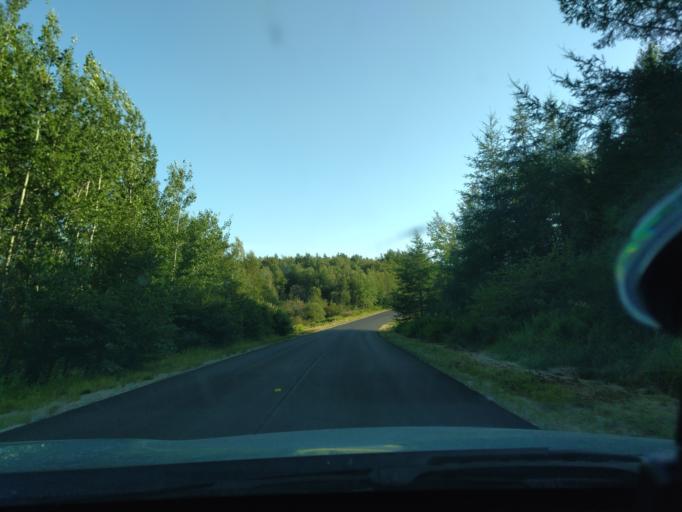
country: US
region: Maine
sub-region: Washington County
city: Eastport
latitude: 44.7193
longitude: -67.1348
